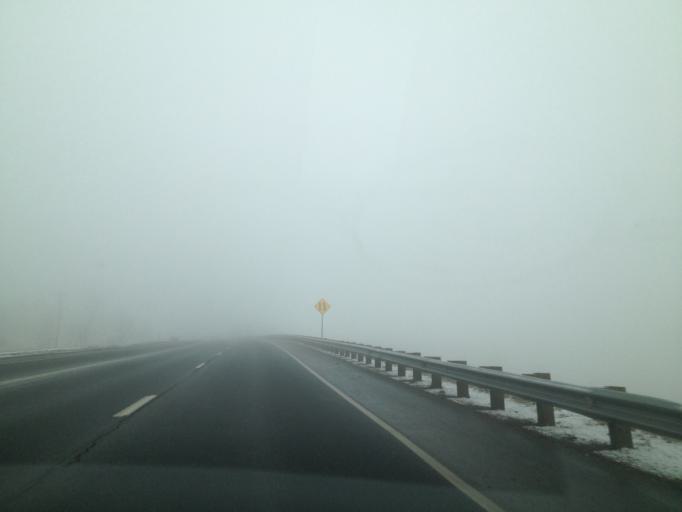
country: US
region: Colorado
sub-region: Boulder County
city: Superior
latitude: 39.9375
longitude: -105.2366
